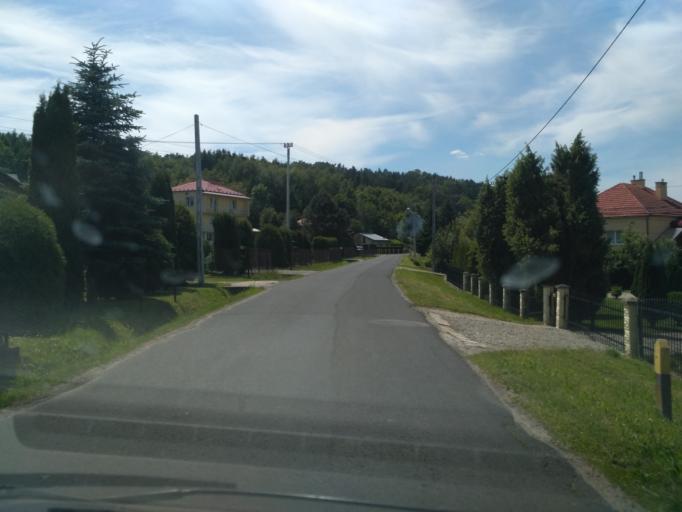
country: PL
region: Subcarpathian Voivodeship
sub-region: Powiat strzyzowski
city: Strzyzow
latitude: 49.8620
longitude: 21.7798
